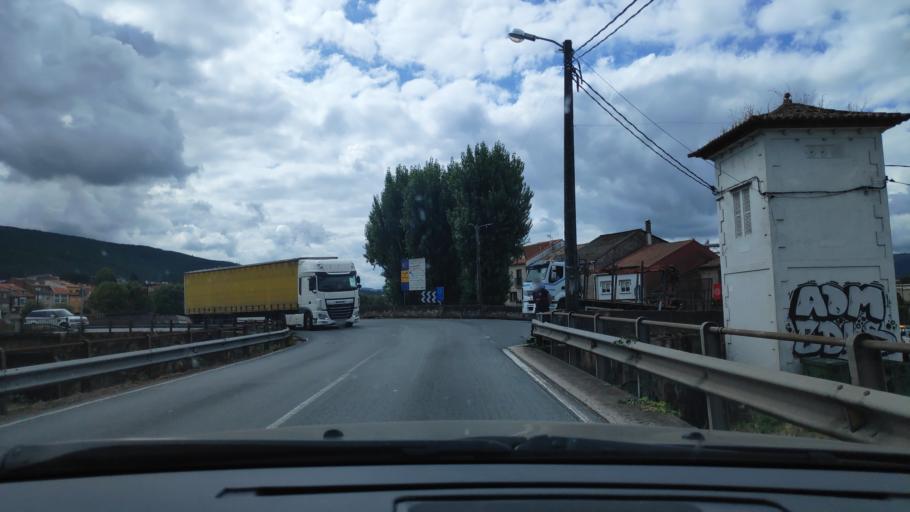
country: ES
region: Galicia
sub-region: Provincia da Coruna
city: Padron
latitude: 42.7259
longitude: -8.6560
